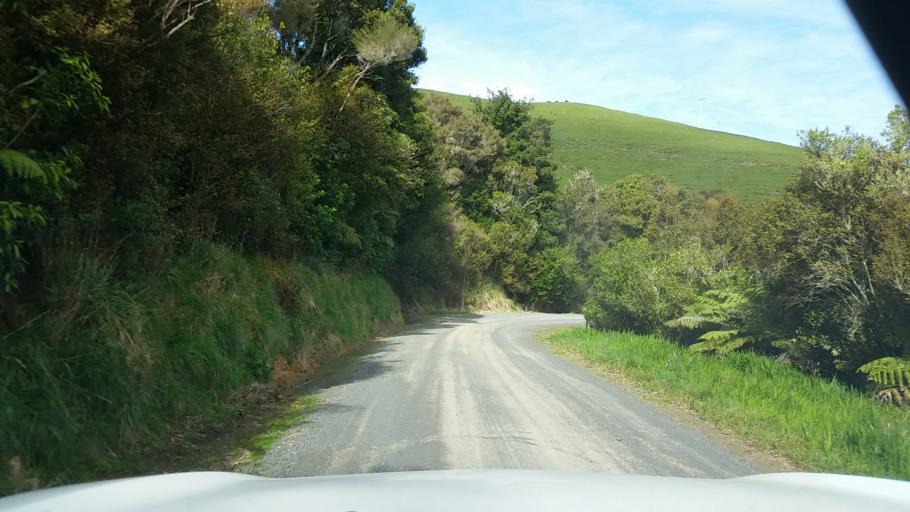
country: NZ
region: Waikato
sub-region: Hauraki District
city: Ngatea
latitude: -37.4784
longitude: 175.4544
